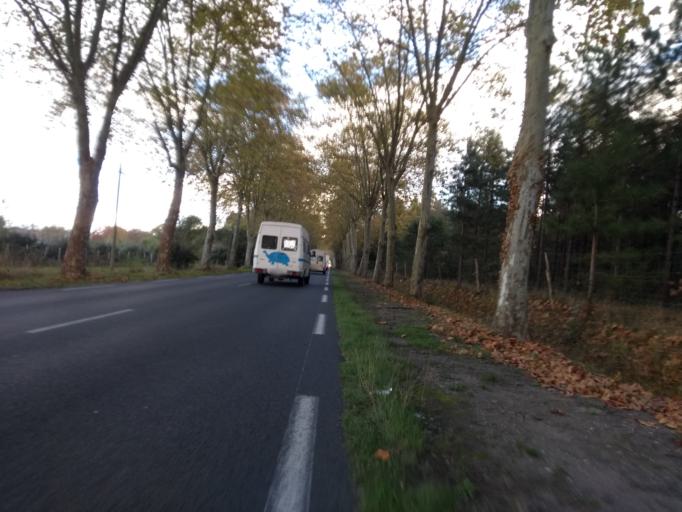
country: FR
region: Aquitaine
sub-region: Departement de la Gironde
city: Cestas
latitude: 44.7030
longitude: -0.7039
